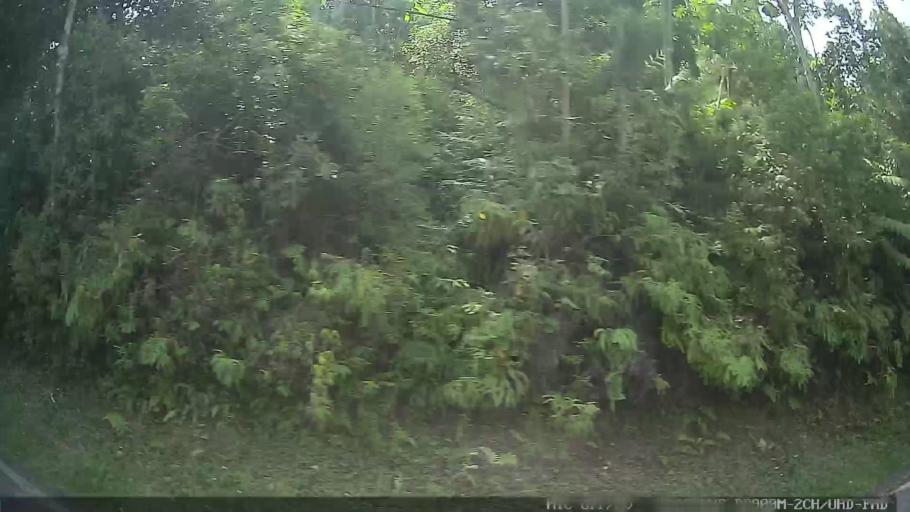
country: BR
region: Sao Paulo
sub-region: Ribeirao Pires
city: Ribeirao Pires
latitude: -23.6787
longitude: -46.3838
